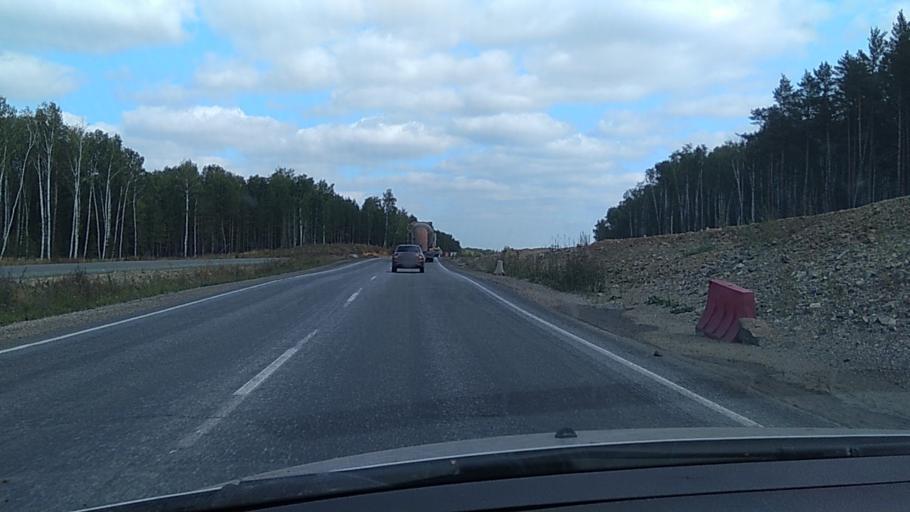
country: RU
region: Chelyabinsk
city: Chebarkul'
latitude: 54.9232
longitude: 60.2809
